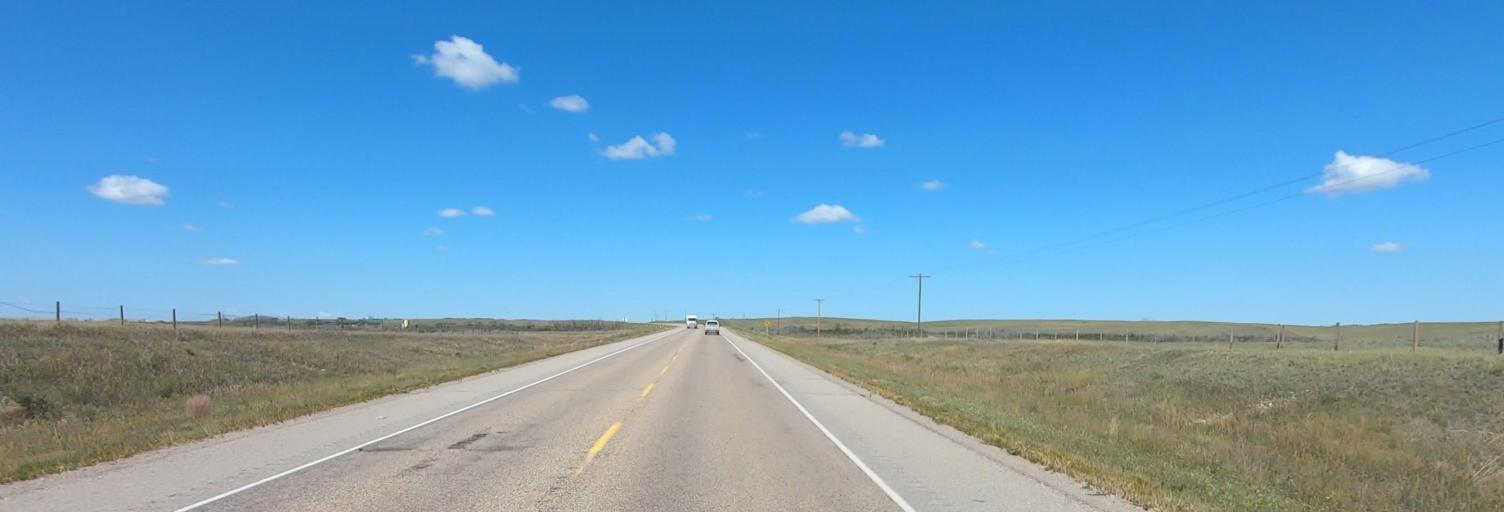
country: CA
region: Alberta
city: Strathmore
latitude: 50.8688
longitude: -113.1524
